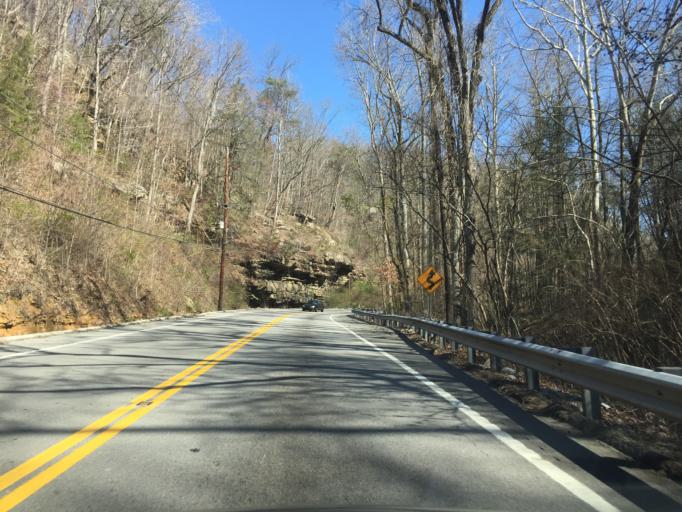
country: US
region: Tennessee
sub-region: Hamilton County
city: Signal Mountain
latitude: 35.1173
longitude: -85.3541
